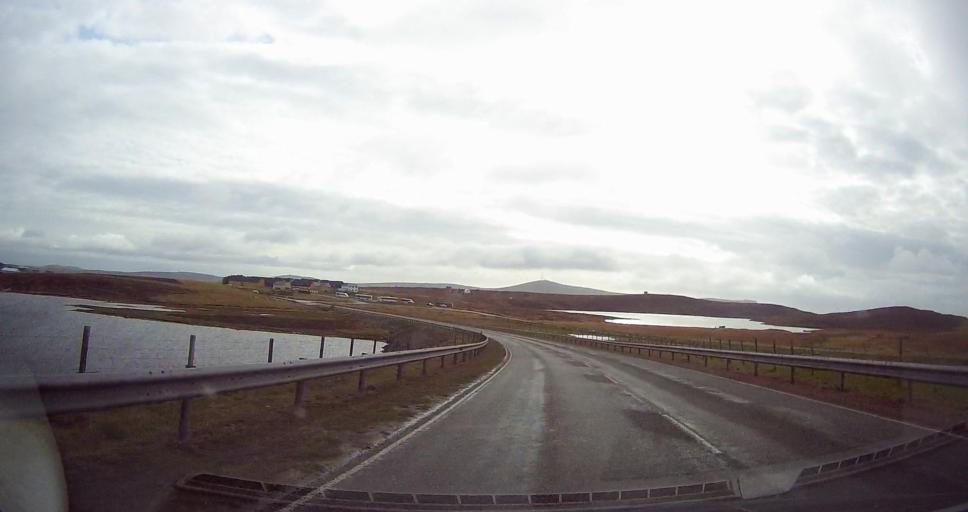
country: GB
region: Scotland
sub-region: Shetland Islands
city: Lerwick
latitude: 60.1387
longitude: -1.1964
